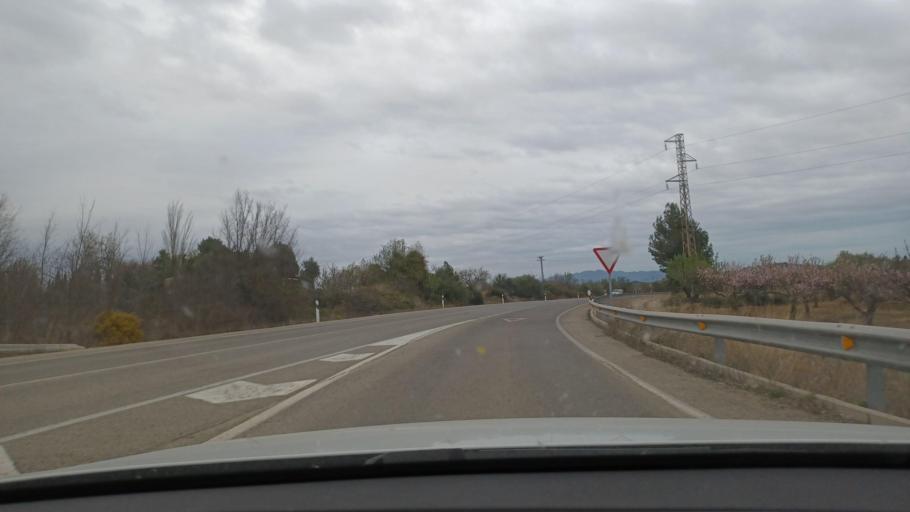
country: ES
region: Valencia
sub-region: Provincia de Castello
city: Traiguera
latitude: 40.5240
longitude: 0.2952
